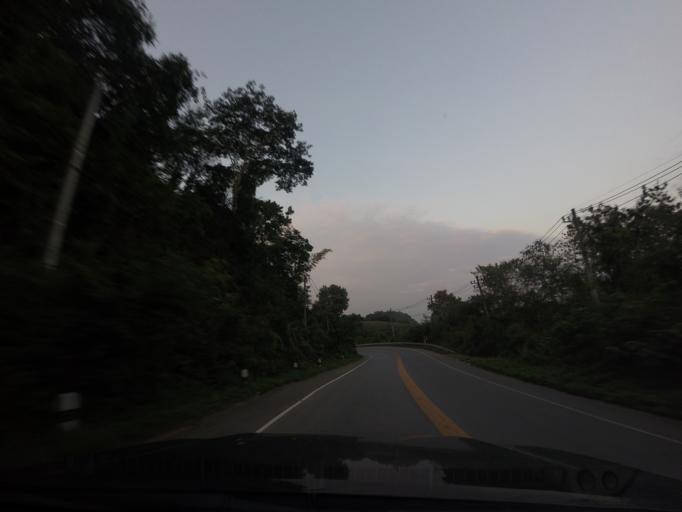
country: TH
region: Nan
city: Na Noi
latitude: 18.4501
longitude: 100.7131
